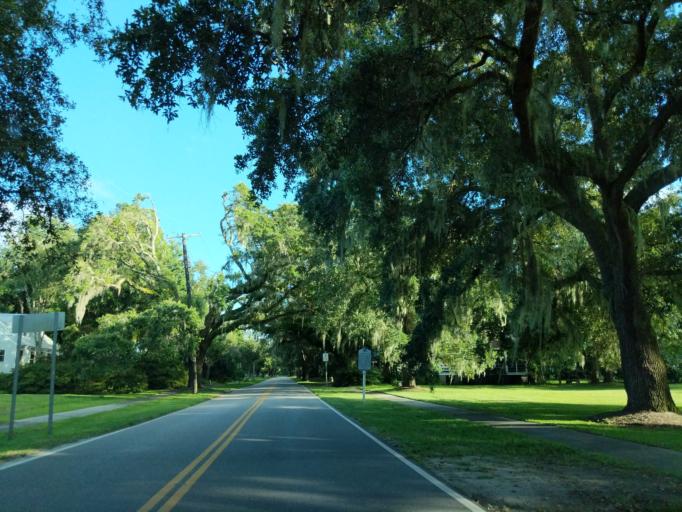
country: US
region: South Carolina
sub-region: Charleston County
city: Awendaw
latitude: 33.0856
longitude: -79.4607
